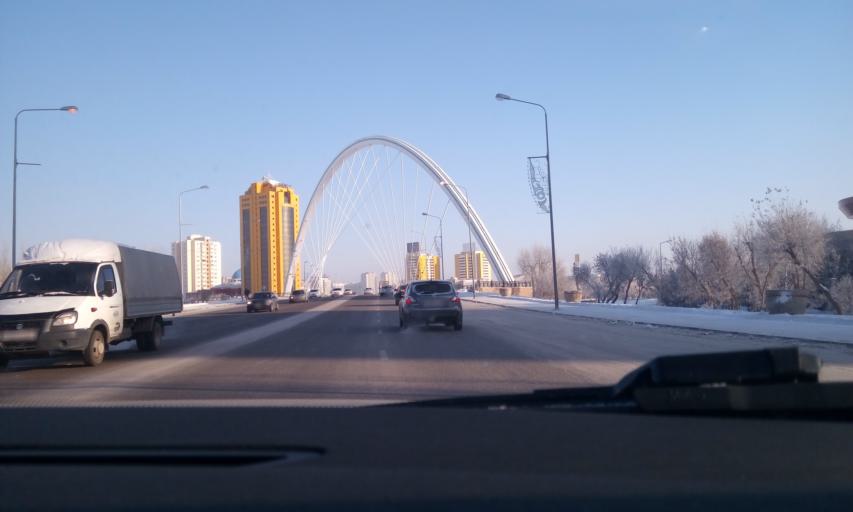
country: KZ
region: Astana Qalasy
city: Astana
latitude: 51.1501
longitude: 71.4258
